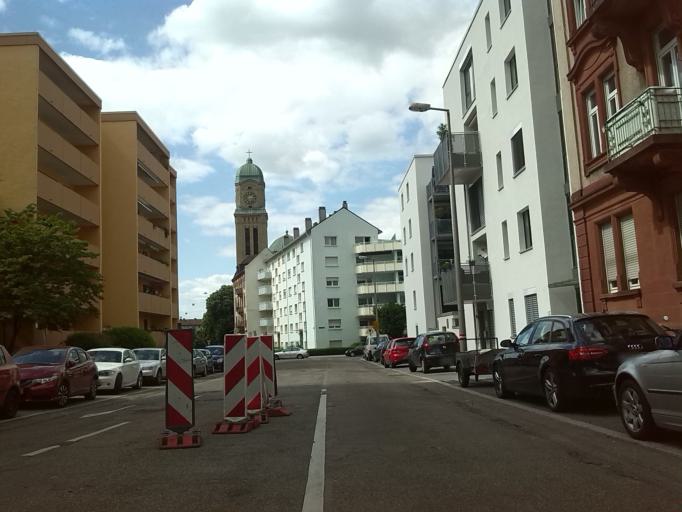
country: DE
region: Baden-Wuerttemberg
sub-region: Karlsruhe Region
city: Mannheim
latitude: 49.4970
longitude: 8.4915
